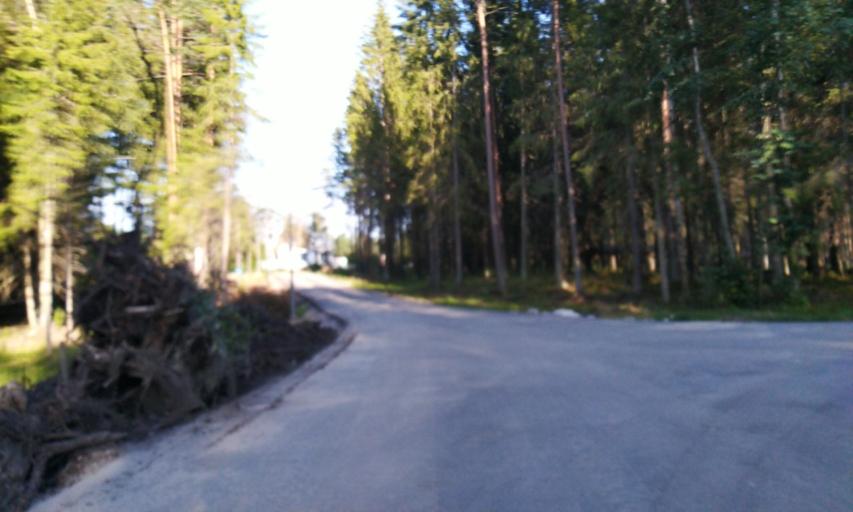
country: RU
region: Leningrad
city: Toksovo
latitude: 60.1339
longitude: 30.4571
